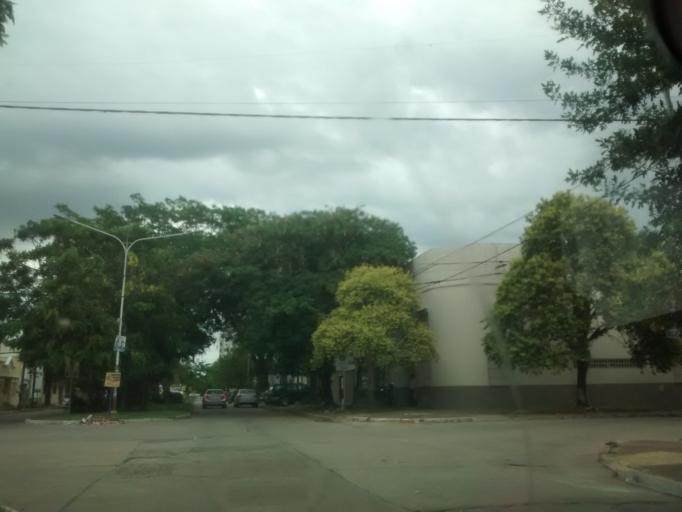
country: AR
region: Chaco
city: Resistencia
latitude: -27.4442
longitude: -58.9876
